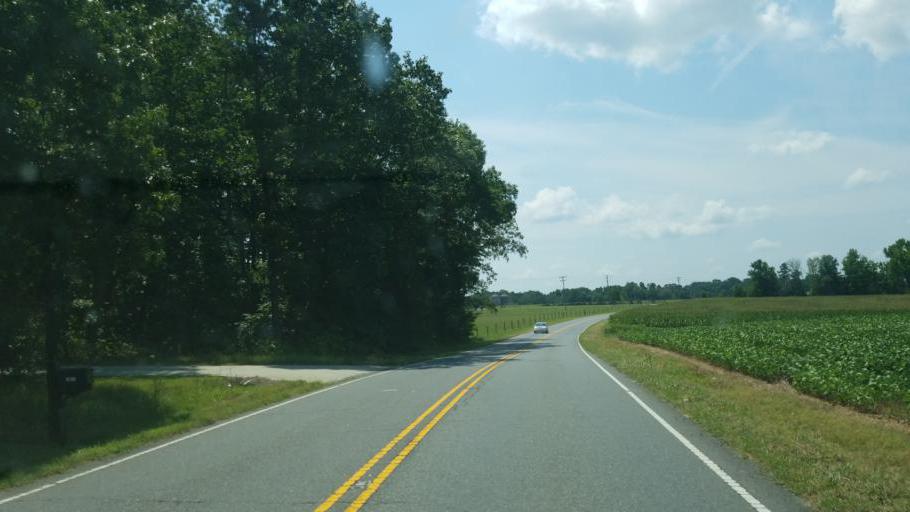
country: US
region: North Carolina
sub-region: Cleveland County
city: Kings Mountain
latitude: 35.2972
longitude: -81.3558
